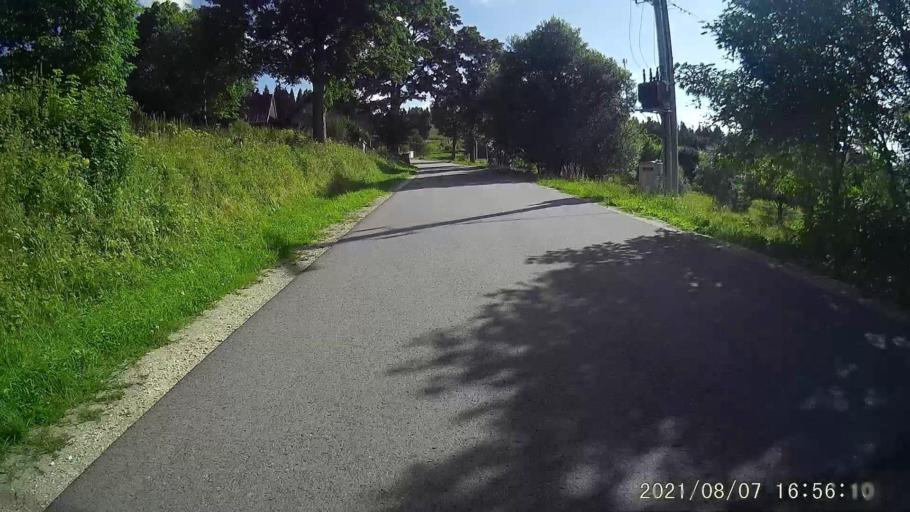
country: PL
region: Lower Silesian Voivodeship
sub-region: Powiat klodzki
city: Bystrzyca Klodzka
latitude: 50.2803
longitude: 16.5407
